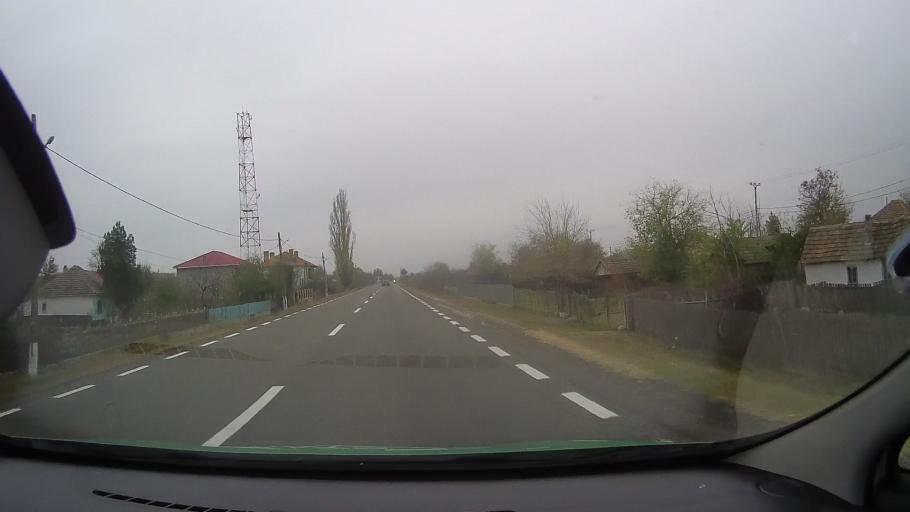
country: RO
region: Ialomita
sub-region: Comuna Giurgeni
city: Giurgeni
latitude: 44.7479
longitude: 27.8571
